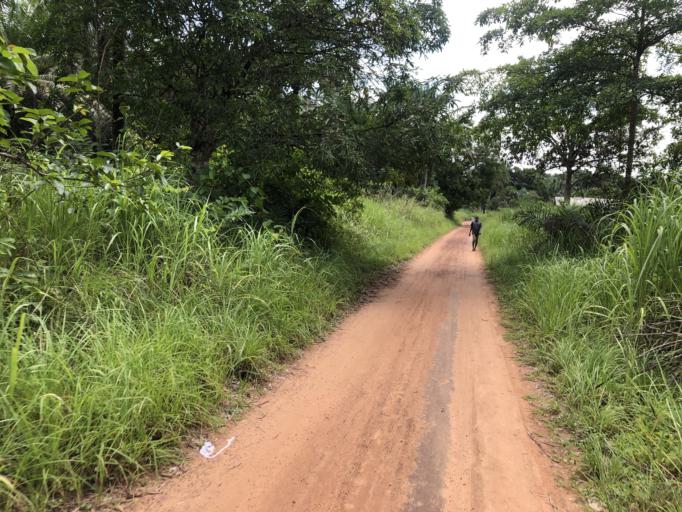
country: SL
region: Northern Province
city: Lunsar
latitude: 8.7140
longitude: -12.5184
